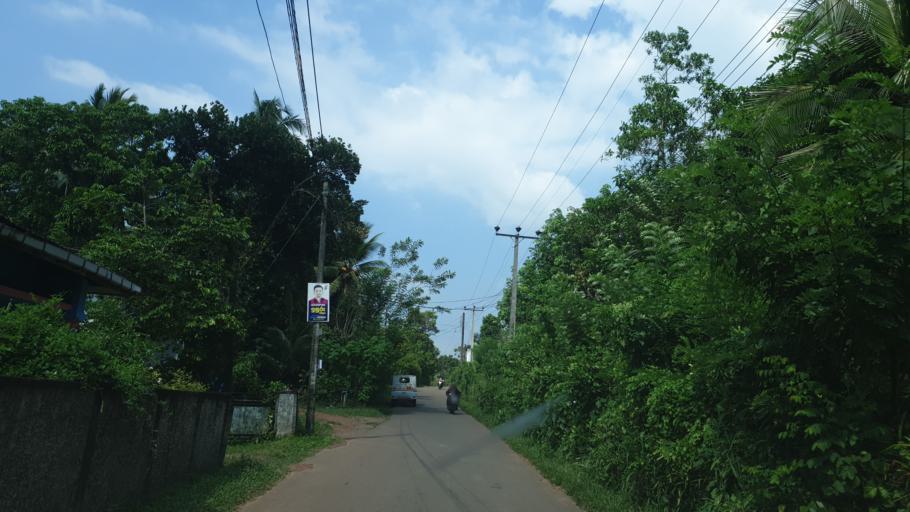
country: LK
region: Western
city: Panadura
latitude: 6.7360
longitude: 79.9517
